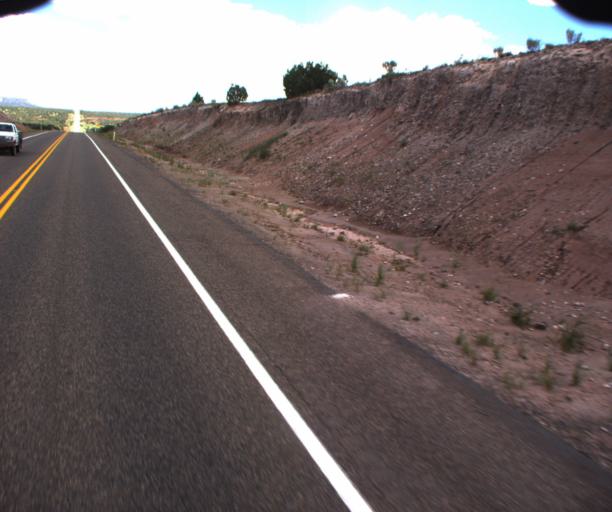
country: US
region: Arizona
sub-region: Apache County
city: Springerville
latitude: 34.1550
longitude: -109.1338
